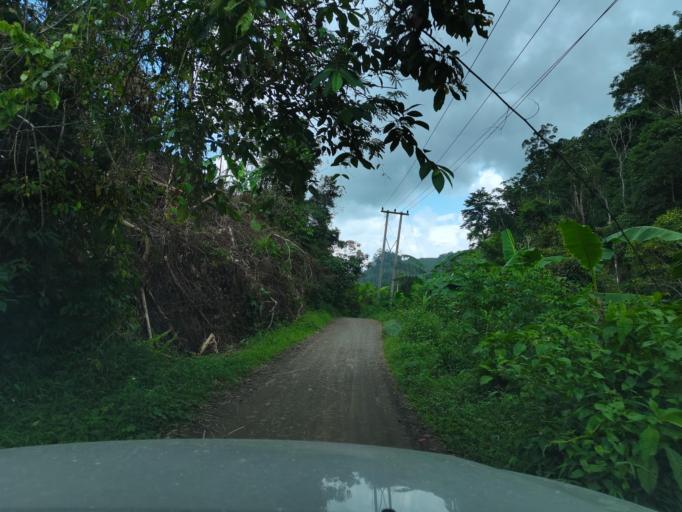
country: LA
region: Loungnamtha
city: Muang Long
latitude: 20.7749
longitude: 101.0170
